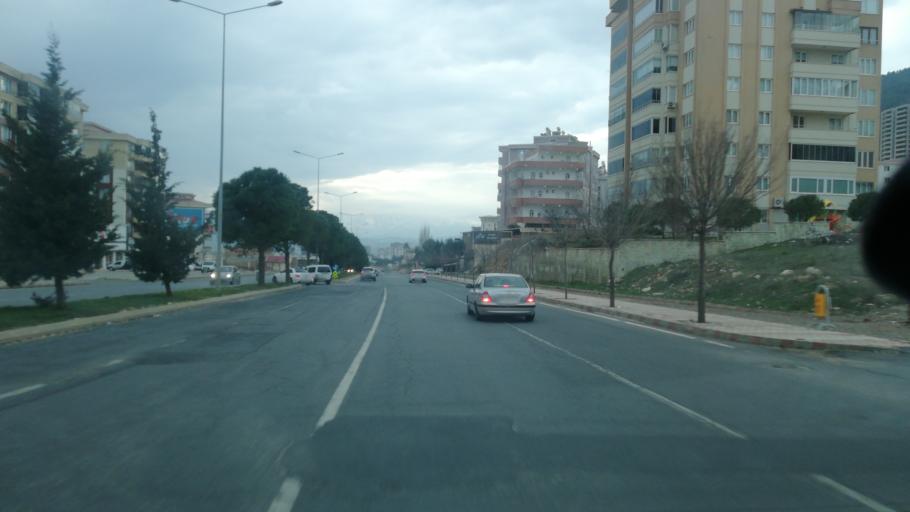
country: TR
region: Kahramanmaras
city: Kahramanmaras
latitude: 37.5974
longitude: 36.8464
